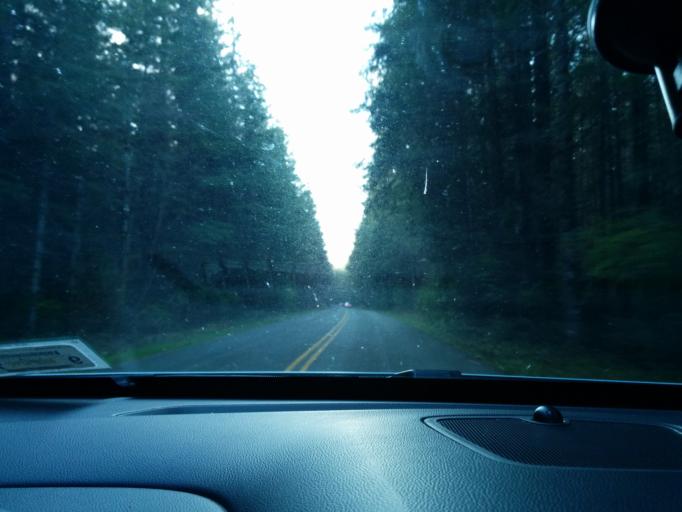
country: US
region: Washington
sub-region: Snohomish County
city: Gold Bar
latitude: 47.8936
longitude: -121.7405
